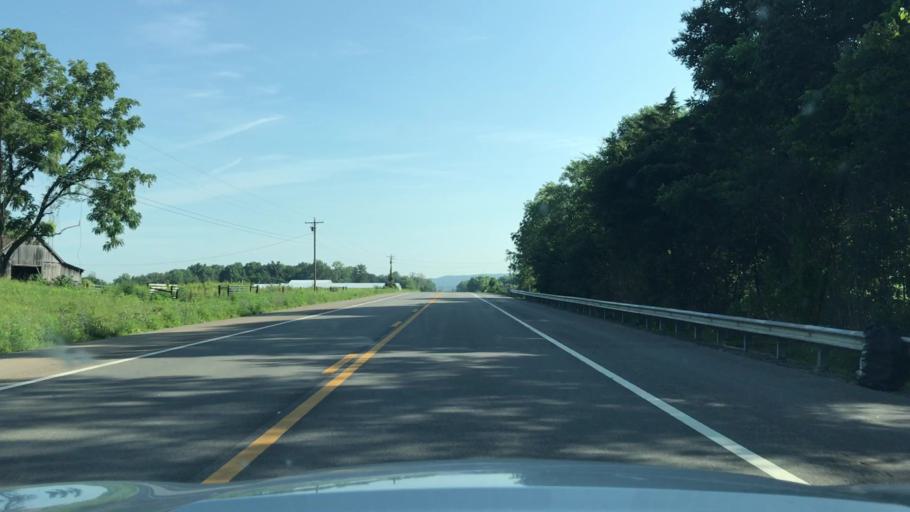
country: US
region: Tennessee
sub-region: Pickett County
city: Byrdstown
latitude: 36.5075
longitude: -85.1738
